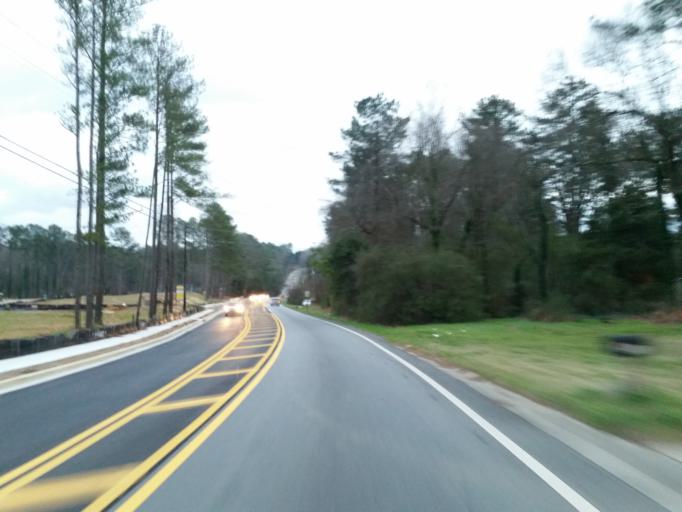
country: US
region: Georgia
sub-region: Cobb County
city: Fair Oaks
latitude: 33.8742
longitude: -84.5798
